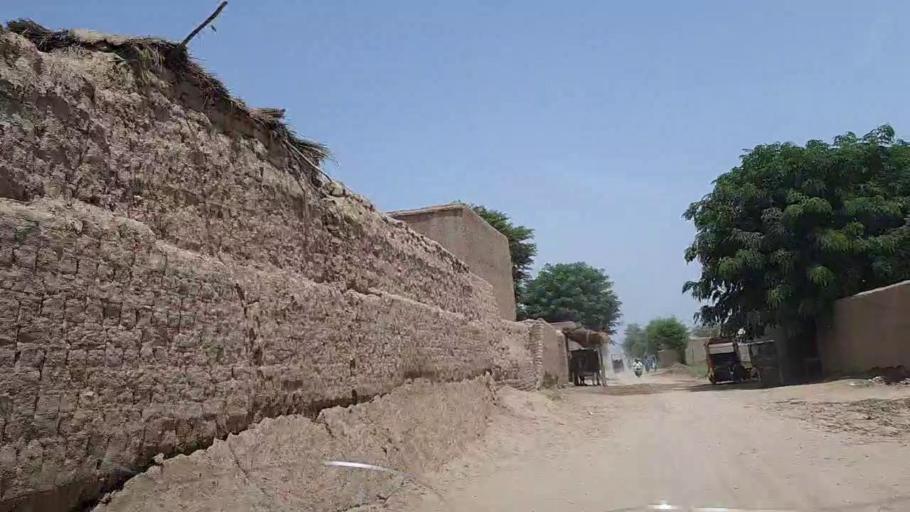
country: PK
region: Sindh
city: Tharu Shah
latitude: 26.9042
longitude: 68.0062
